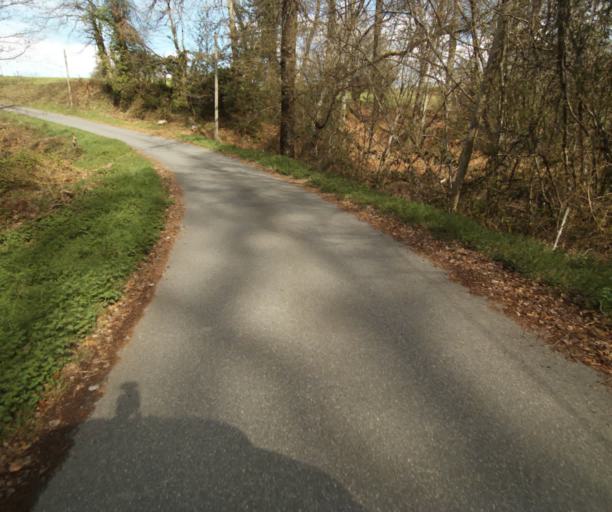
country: FR
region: Limousin
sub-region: Departement de la Correze
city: Correze
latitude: 45.3458
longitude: 1.8607
